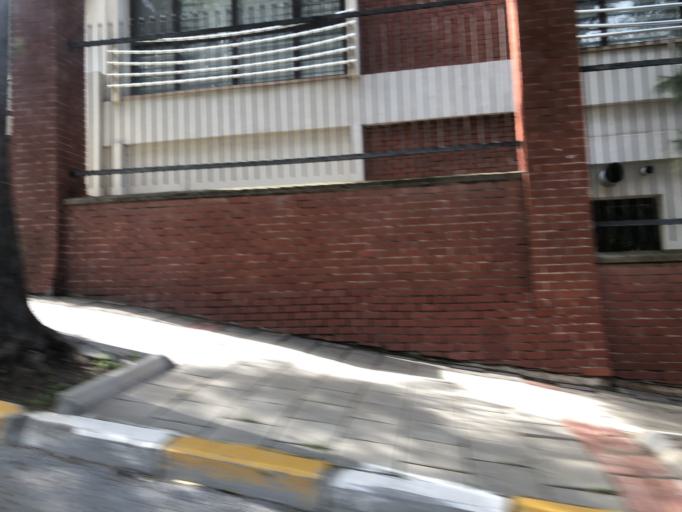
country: TR
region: Izmir
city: Karabaglar
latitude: 38.3883
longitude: 27.0458
